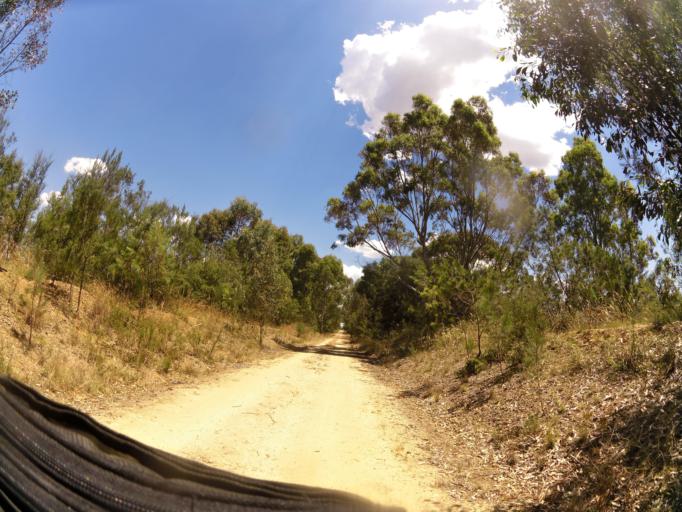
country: AU
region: Victoria
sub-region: Wellington
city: Heyfield
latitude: -37.9815
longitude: 146.8362
